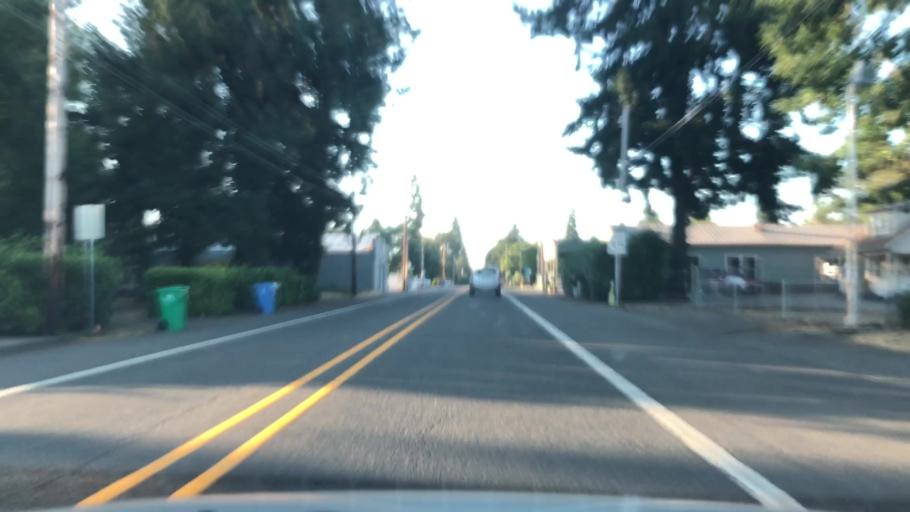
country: US
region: Oregon
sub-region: Clackamas County
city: Oak Grove
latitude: 45.4171
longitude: -122.6455
